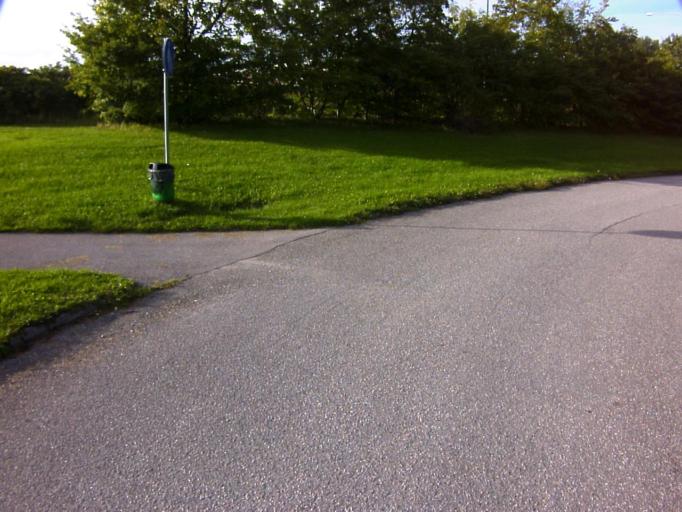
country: SE
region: Soedermanland
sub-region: Eskilstuna Kommun
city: Eskilstuna
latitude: 59.3902
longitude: 16.5339
